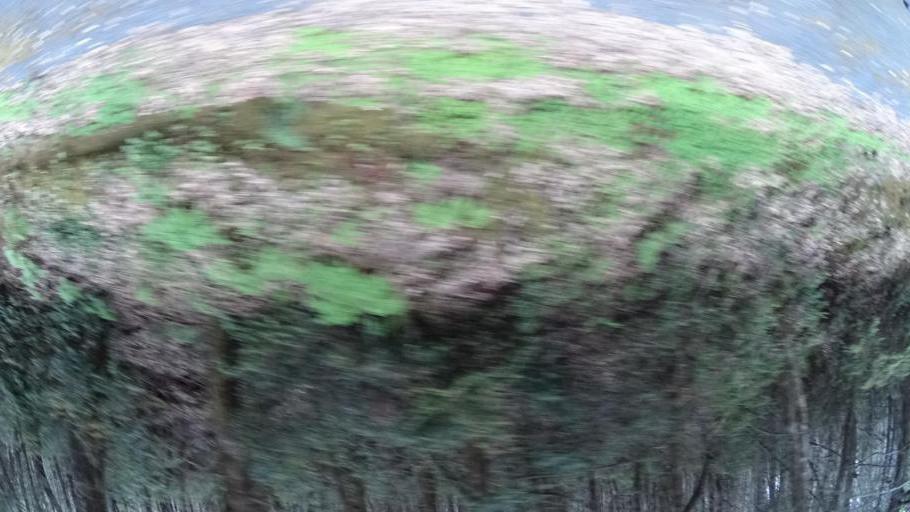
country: US
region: California
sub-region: Humboldt County
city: Willow Creek
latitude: 41.2013
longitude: -123.7675
